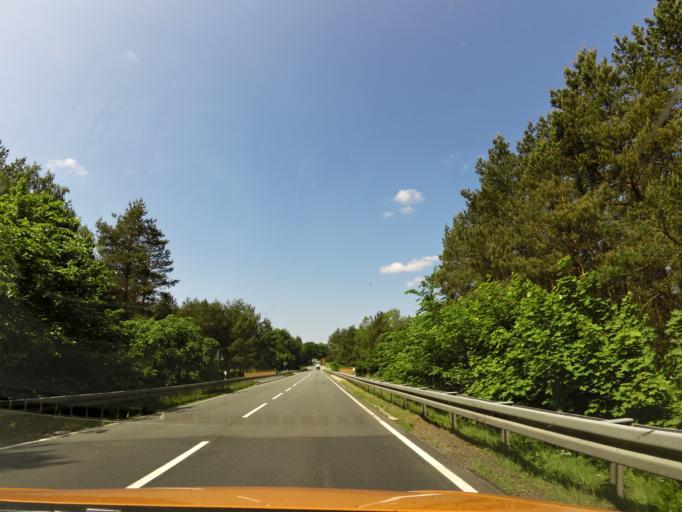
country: DE
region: Mecklenburg-Vorpommern
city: Pinnow
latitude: 53.5902
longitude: 11.5586
